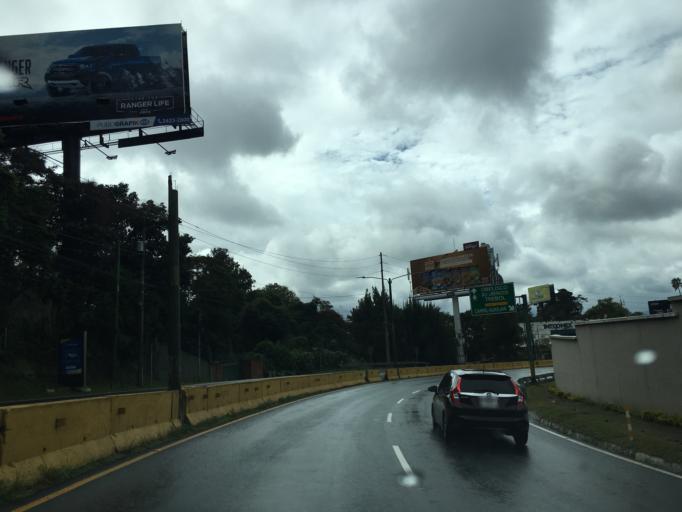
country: GT
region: Guatemala
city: Santa Catarina Pinula
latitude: 14.5772
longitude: -90.4894
